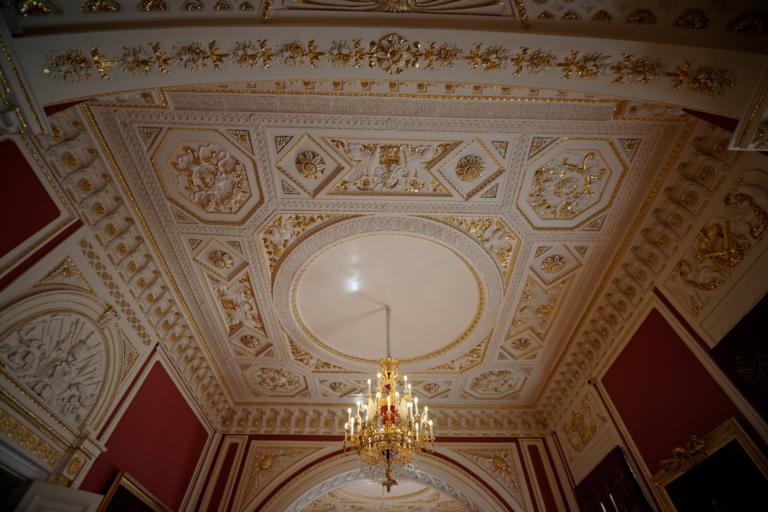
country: RU
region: St.-Petersburg
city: Saint Petersburg
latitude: 59.9406
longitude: 30.3374
